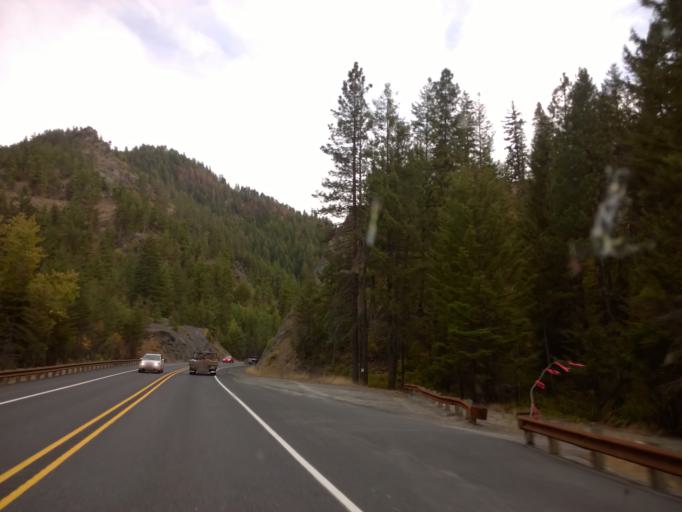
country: US
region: Washington
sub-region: Chelan County
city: Leavenworth
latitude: 47.4318
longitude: -120.6562
